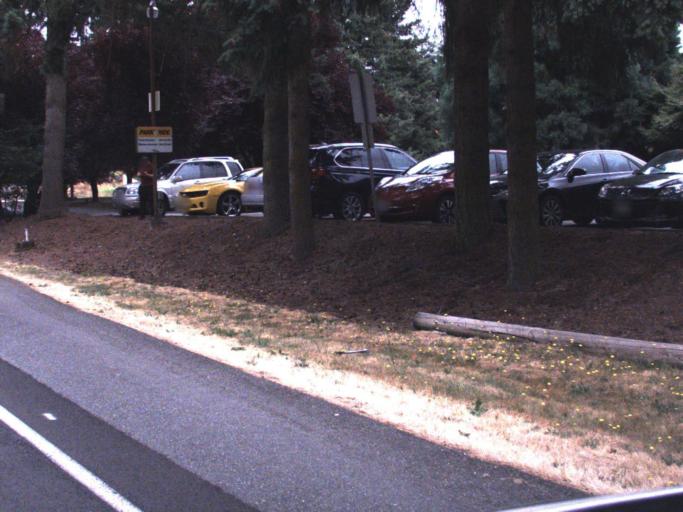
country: US
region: Washington
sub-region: King County
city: Redmond
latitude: 47.7030
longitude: -122.1320
